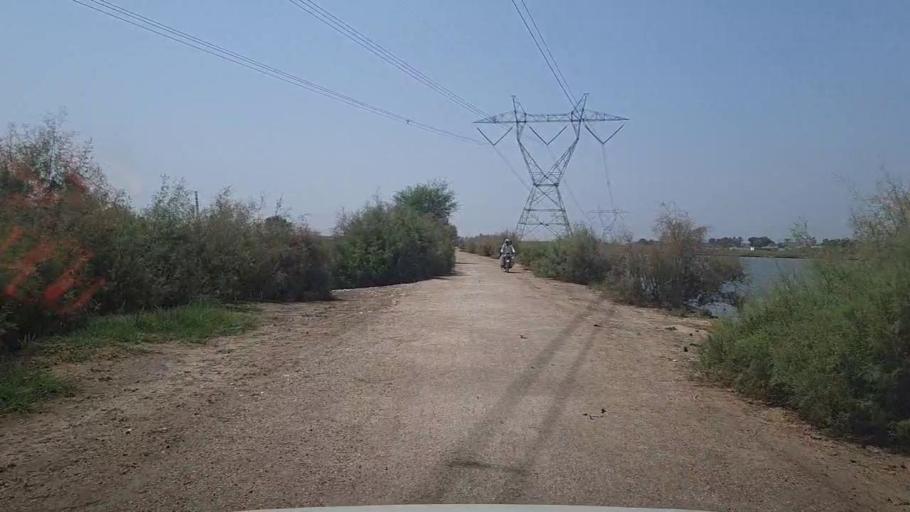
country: PK
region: Sindh
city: Kandhkot
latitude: 28.3190
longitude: 69.3726
